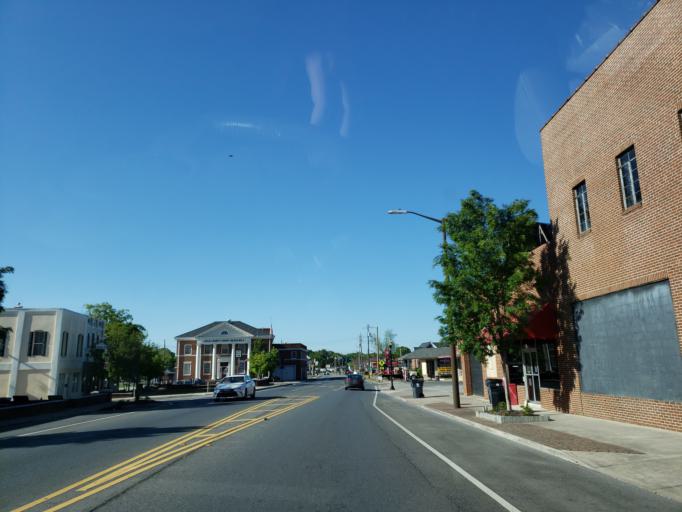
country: US
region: Georgia
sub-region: Polk County
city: Cedartown
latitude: 34.0125
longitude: -85.2549
